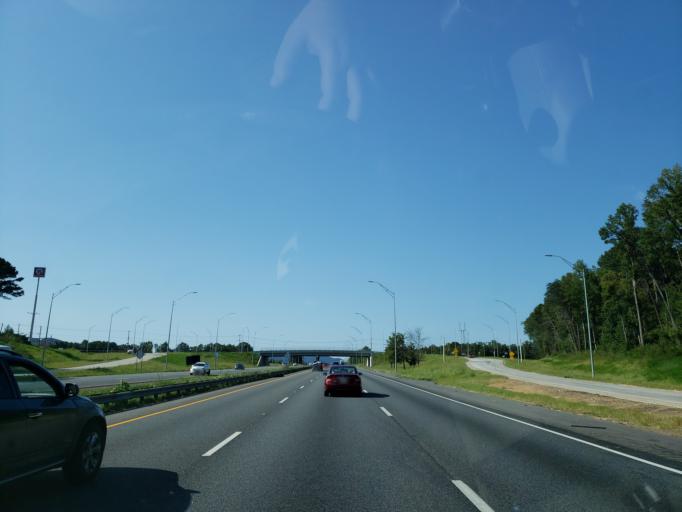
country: US
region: Georgia
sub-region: Whitfield County
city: Dalton
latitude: 34.6510
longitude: -84.9828
